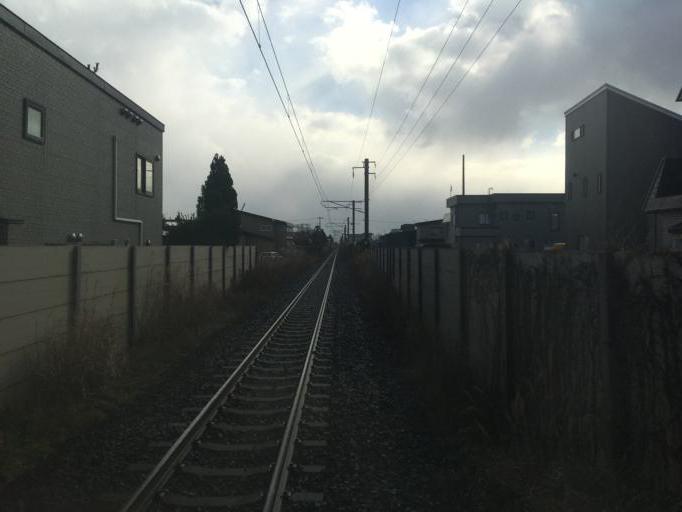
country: JP
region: Aomori
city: Aomori Shi
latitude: 40.8614
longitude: 140.6870
